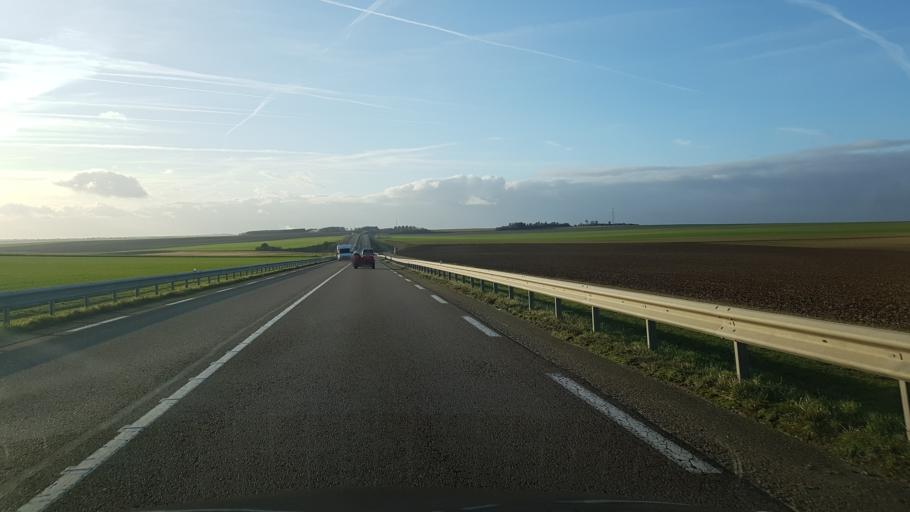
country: FR
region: Champagne-Ardenne
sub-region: Departement de l'Aube
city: Mailly-le-Camp
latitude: 48.7326
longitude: 4.2600
